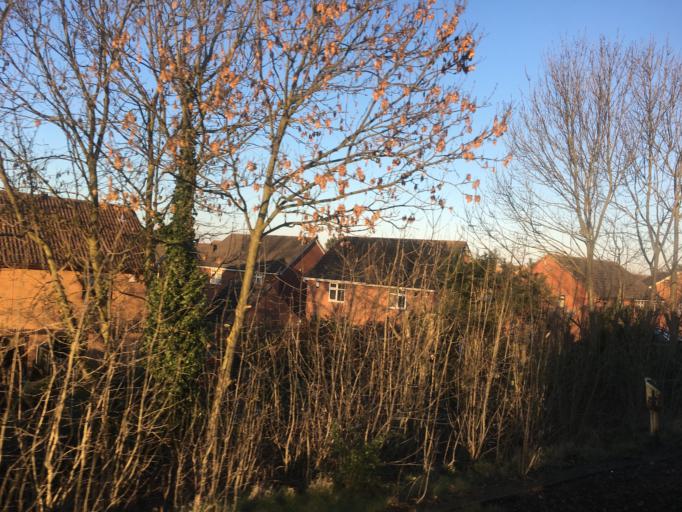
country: GB
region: England
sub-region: Derbyshire
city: Long Eaton
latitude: 52.8852
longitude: -1.2912
